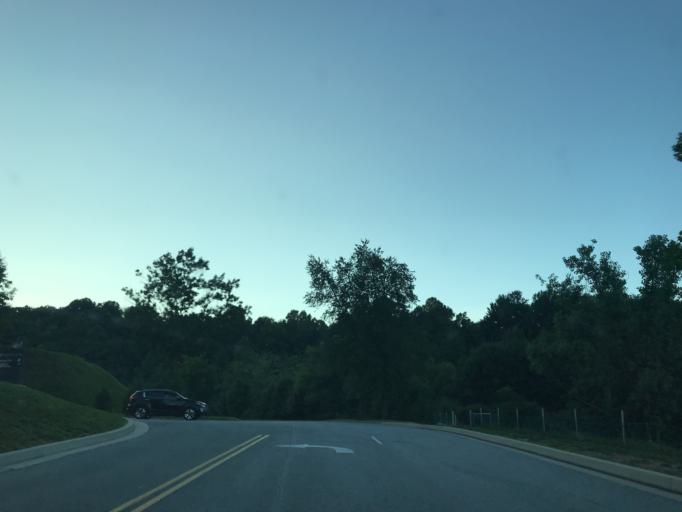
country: US
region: Maryland
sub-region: Baltimore County
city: Hunt Valley
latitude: 39.4998
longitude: -76.6519
